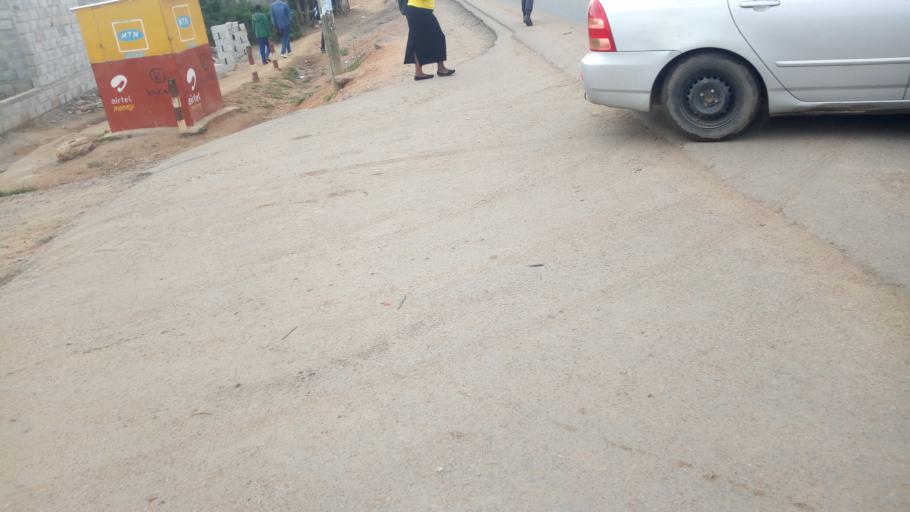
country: ZM
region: Lusaka
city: Lusaka
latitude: -15.3918
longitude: 28.2847
